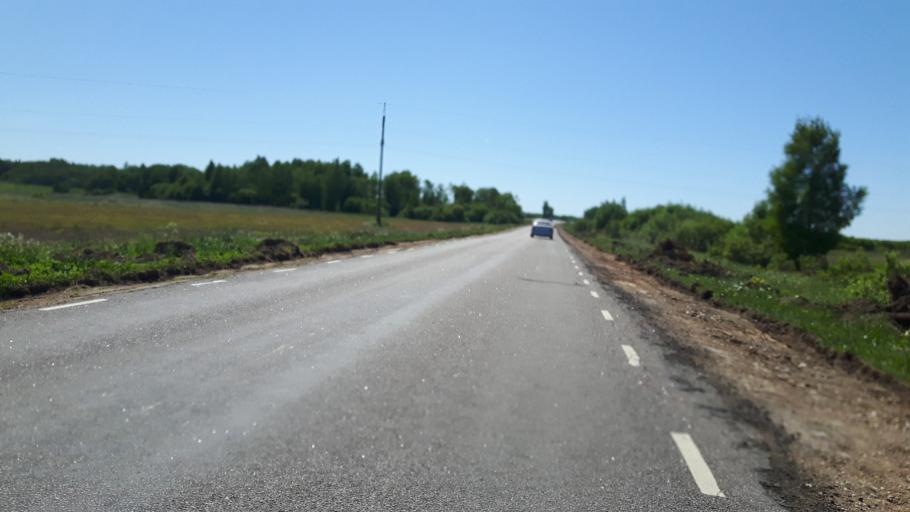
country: EE
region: Ida-Virumaa
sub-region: Narva-Joesuu linn
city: Narva-Joesuu
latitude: 59.3821
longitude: 27.9212
